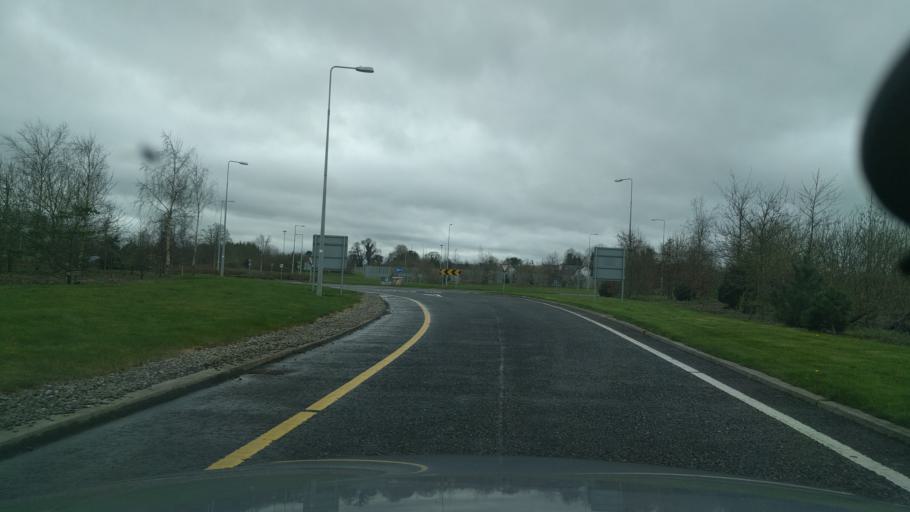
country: IE
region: Leinster
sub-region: An Mhi
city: Enfield
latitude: 53.4122
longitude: -6.8772
